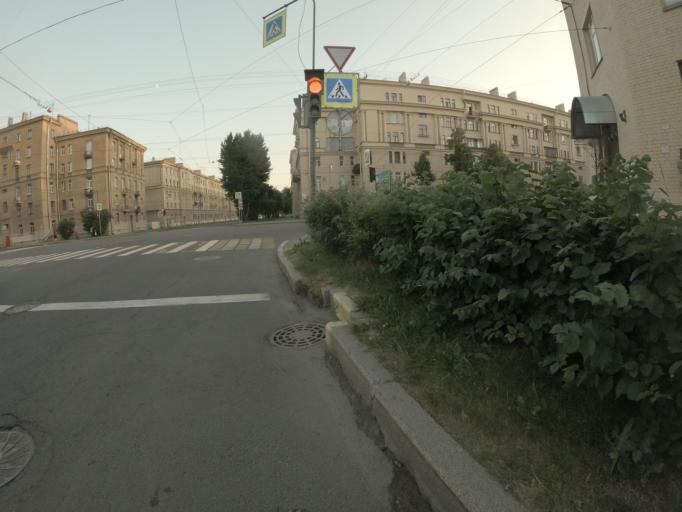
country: RU
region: St.-Petersburg
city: Avtovo
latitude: 59.8724
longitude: 30.2664
